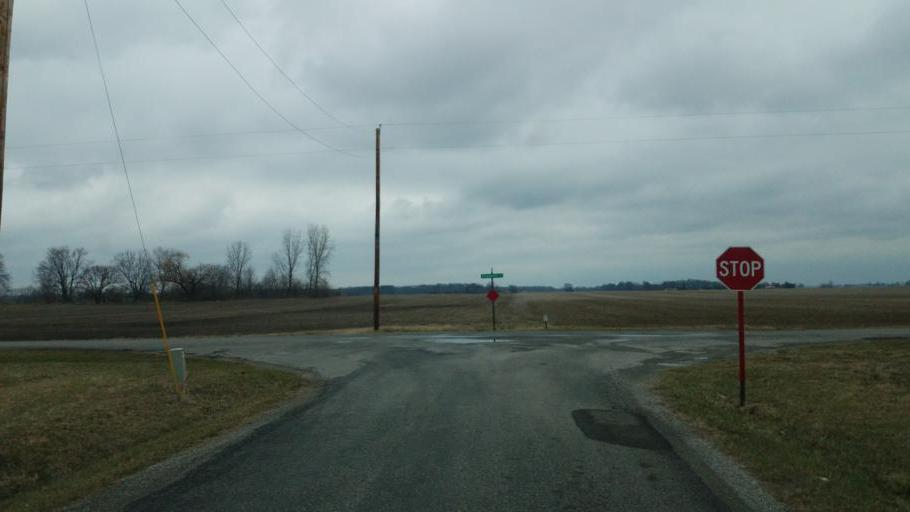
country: US
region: Ohio
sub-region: Delaware County
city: Ashley
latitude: 40.3834
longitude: -82.9858
